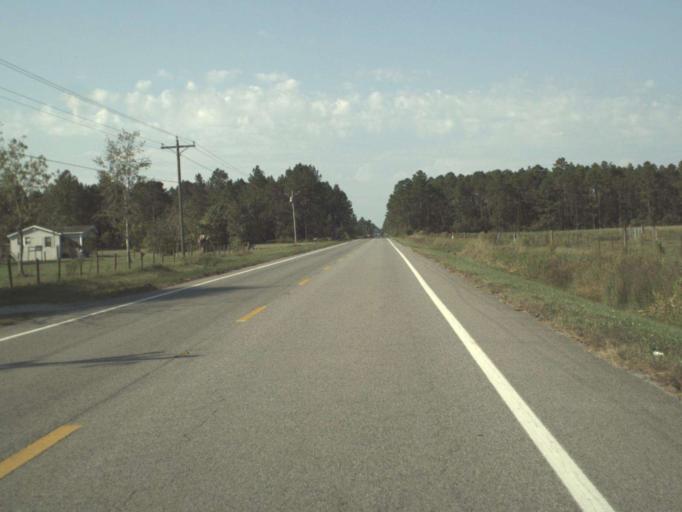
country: US
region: Florida
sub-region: Gulf County
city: Wewahitchka
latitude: 30.0232
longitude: -85.1792
